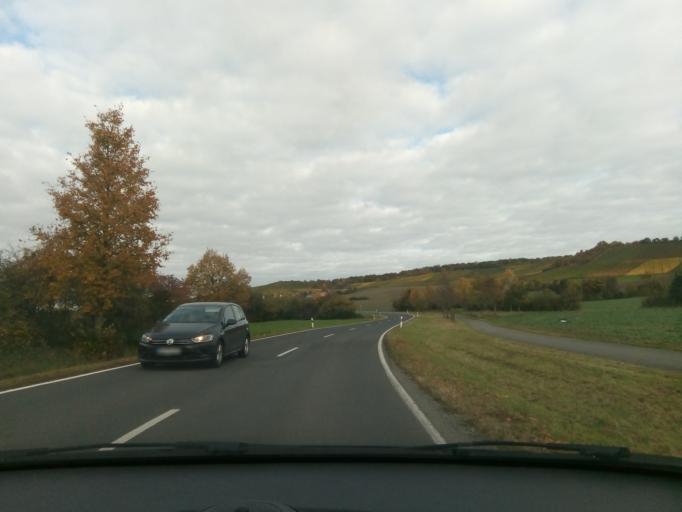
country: DE
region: Bavaria
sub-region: Regierungsbezirk Unterfranken
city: Oberschwarzach
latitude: 49.8748
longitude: 10.3995
